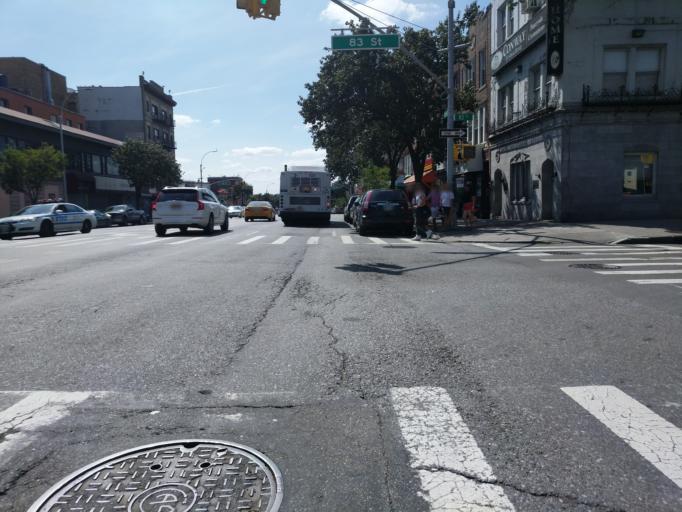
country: US
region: New York
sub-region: Queens County
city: Long Island City
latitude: 40.7557
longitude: -73.8844
